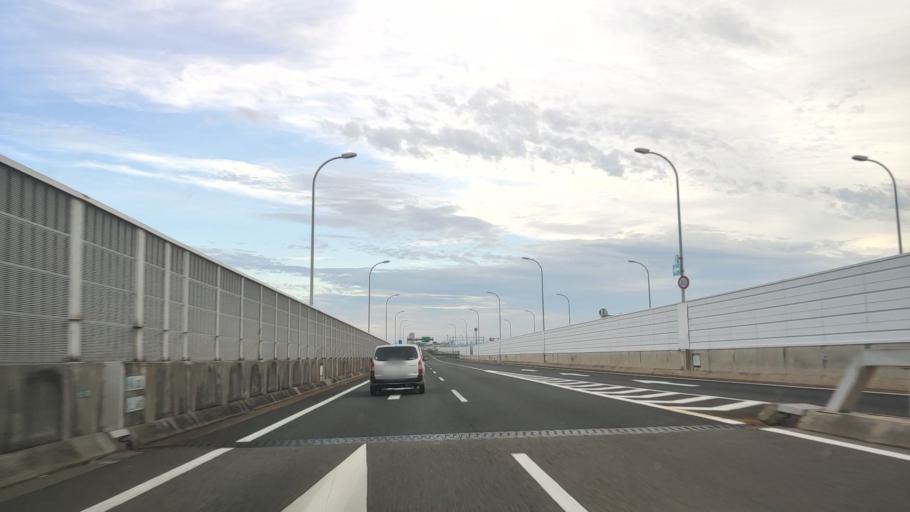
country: JP
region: Aichi
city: Komaki
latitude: 35.2781
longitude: 136.9068
